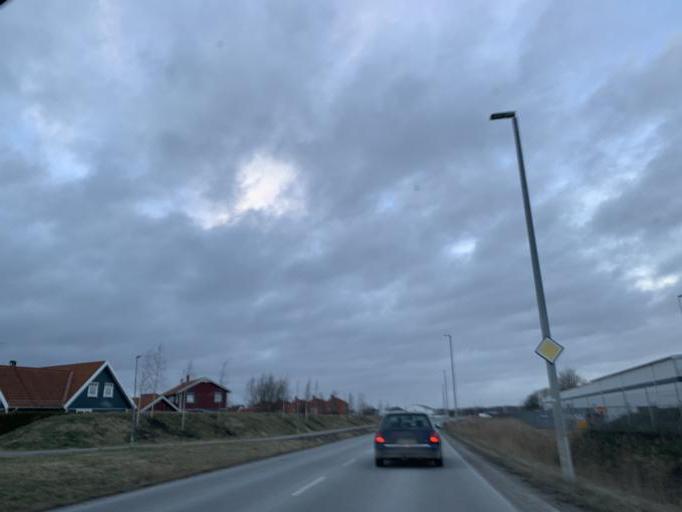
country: SE
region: OErebro
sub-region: Orebro Kommun
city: Orebro
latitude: 59.2596
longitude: 15.2611
